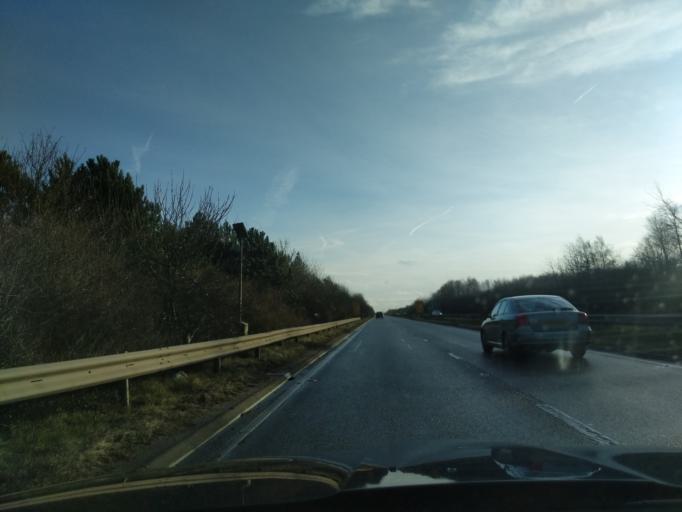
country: GB
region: England
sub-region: Borough of North Tyneside
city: Shiremoor
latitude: 55.0202
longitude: -1.5135
